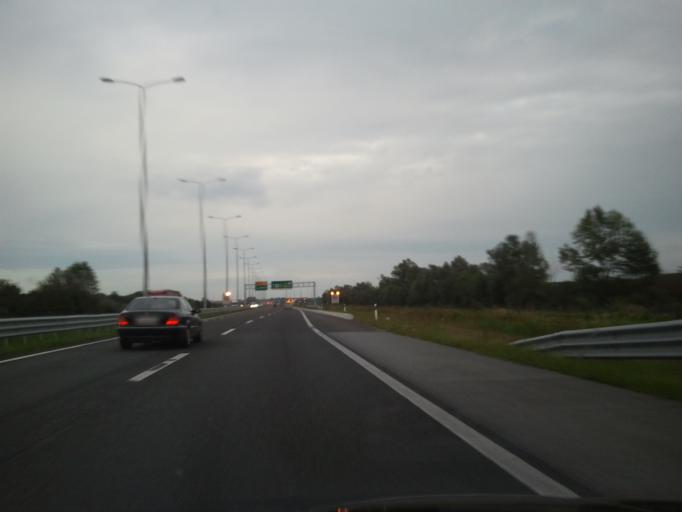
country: HR
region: Zagrebacka
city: Brckovljani
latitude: 45.7558
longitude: 16.2597
